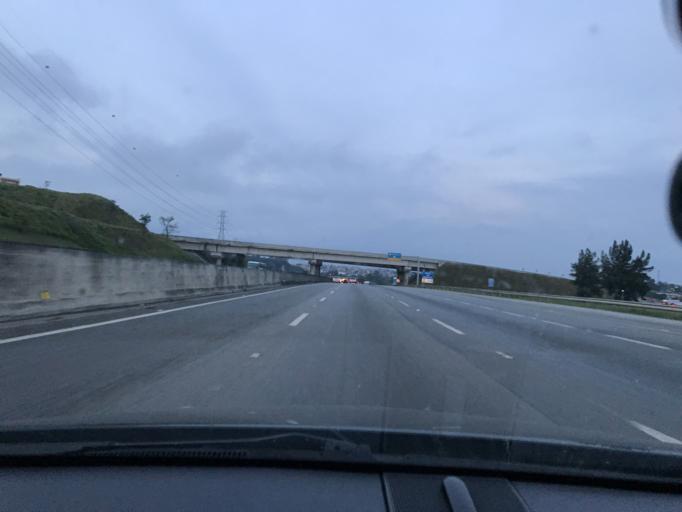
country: BR
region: Sao Paulo
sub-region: Itaquaquecetuba
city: Itaquaquecetuba
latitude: -23.4596
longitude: -46.3420
